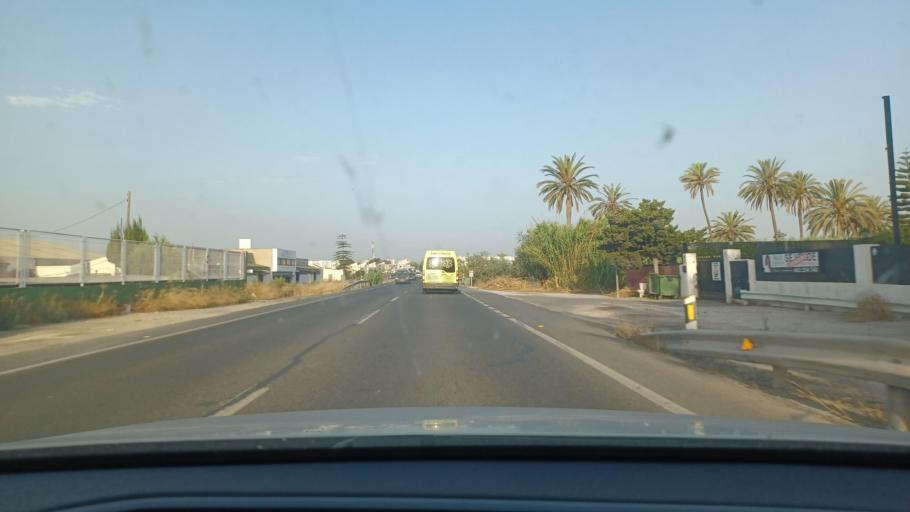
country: ES
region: Valencia
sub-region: Provincia de Alicante
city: Elche
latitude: 38.2761
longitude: -0.6566
